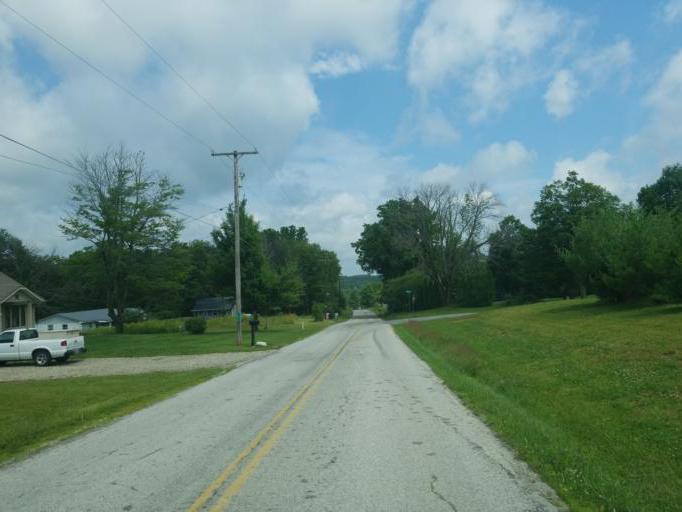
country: US
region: Ohio
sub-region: Richland County
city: Ontario
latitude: 40.7313
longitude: -82.6358
